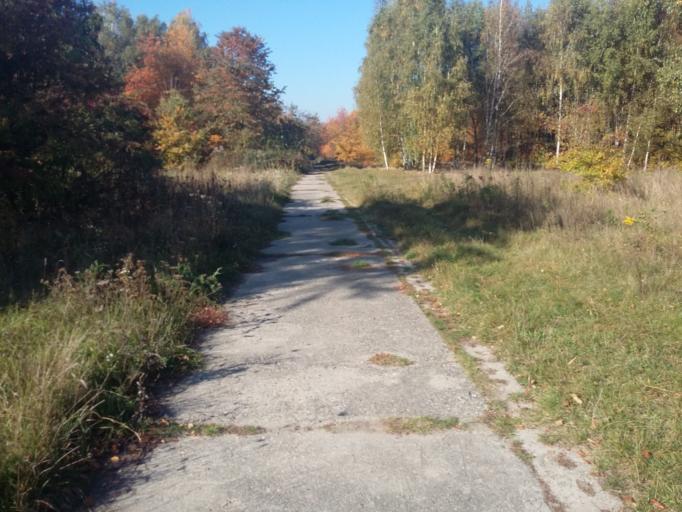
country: PL
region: Lodz Voivodeship
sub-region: Powiat pabianicki
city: Ksawerow
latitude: 51.7289
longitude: 19.4048
